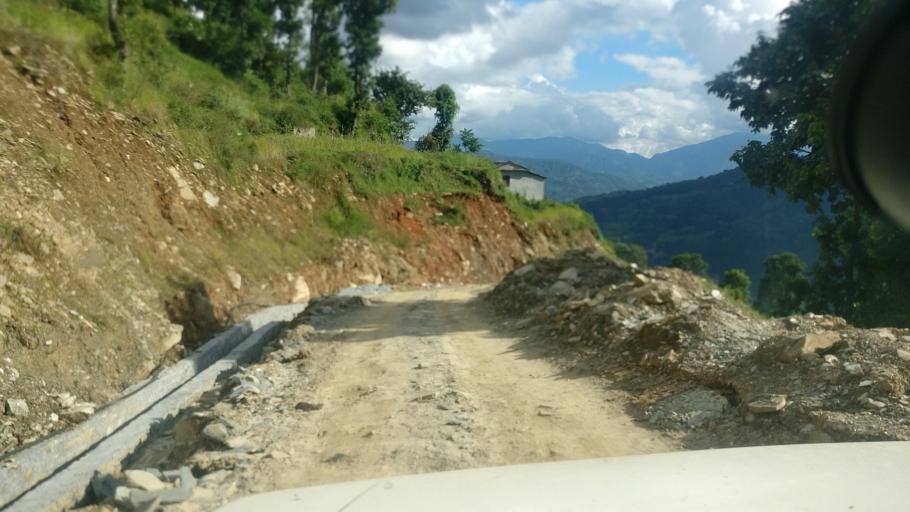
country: NP
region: Western Region
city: Baglung
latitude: 28.2631
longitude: 83.6425
